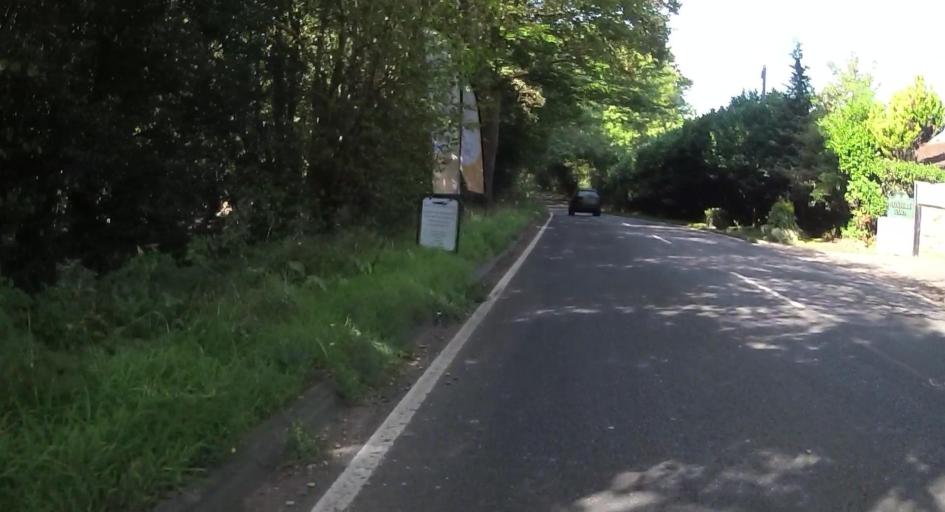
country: GB
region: England
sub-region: Surrey
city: Ottershaw
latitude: 51.3796
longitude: -0.5431
